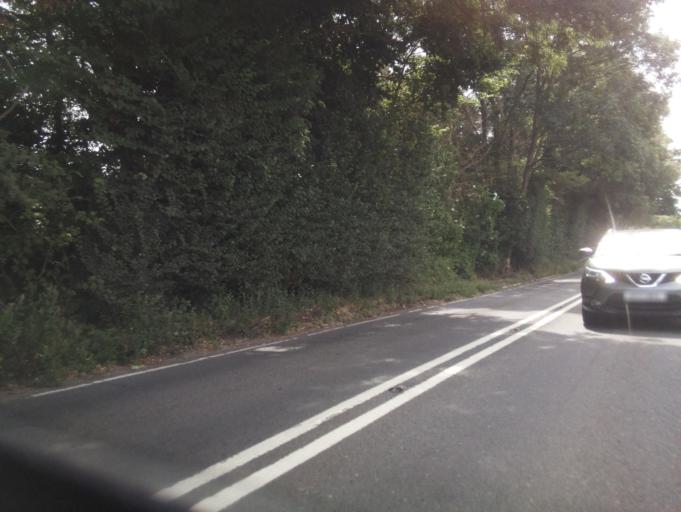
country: GB
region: England
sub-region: Surrey
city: Reigate
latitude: 51.2101
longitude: -0.2006
